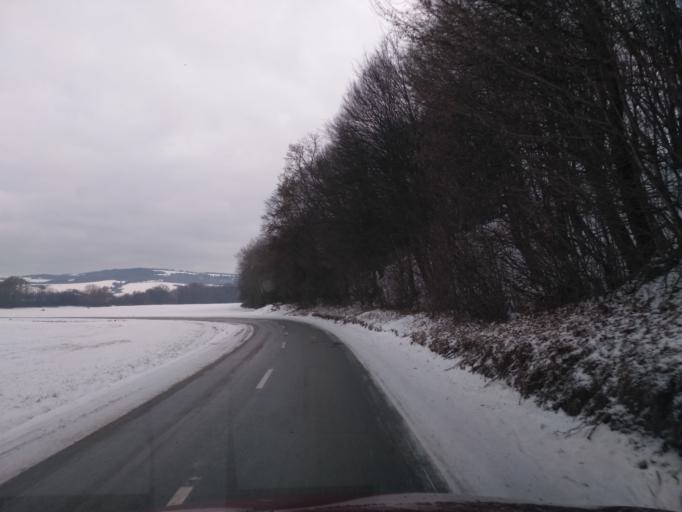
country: SK
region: Presovsky
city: Sabinov
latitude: 49.0533
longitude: 21.0870
